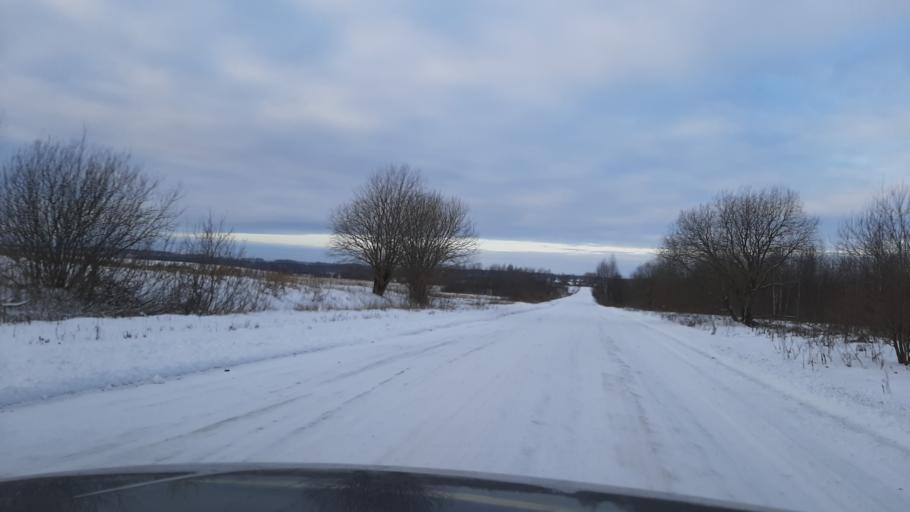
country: RU
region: Kostroma
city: Kosmynino
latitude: 57.4840
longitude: 40.8282
